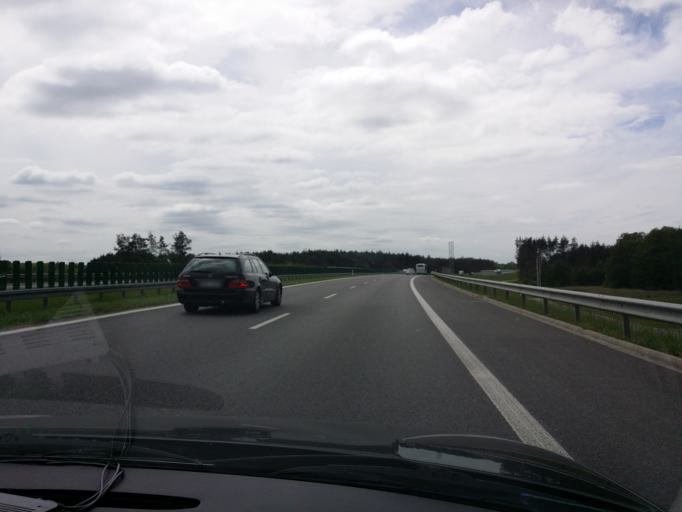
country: PL
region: Masovian Voivodeship
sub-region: Powiat szydlowiecki
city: Oronsko
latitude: 51.3170
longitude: 21.0154
